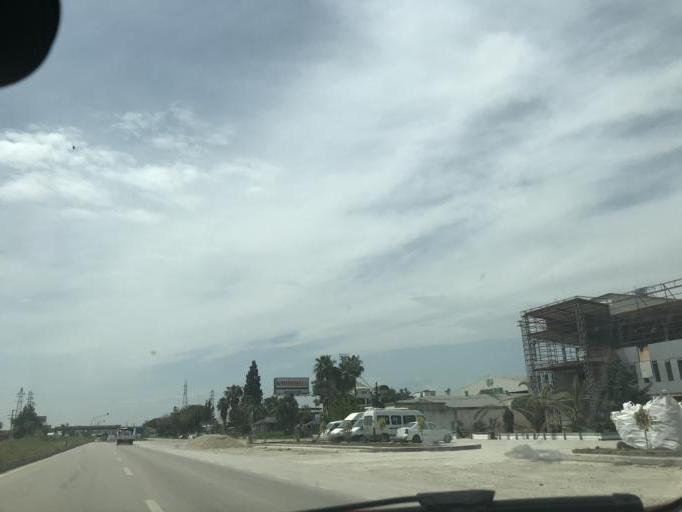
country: TR
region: Adana
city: Yuregir
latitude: 36.9809
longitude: 35.4454
